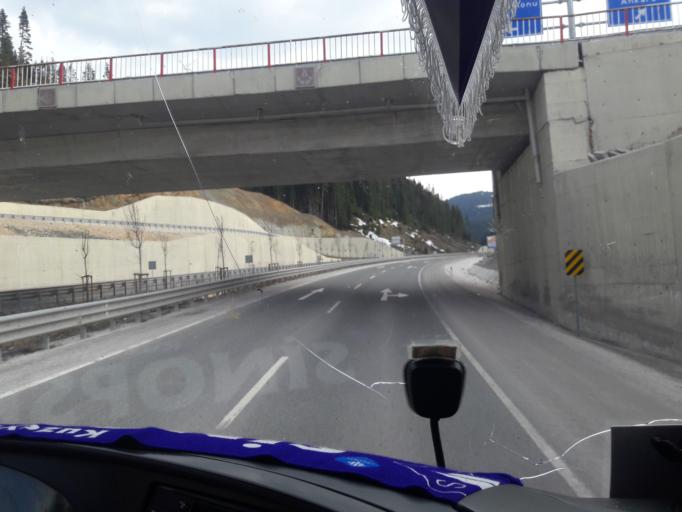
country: TR
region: Kastamonu
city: Kuzyaka
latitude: 41.1010
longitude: 33.7512
